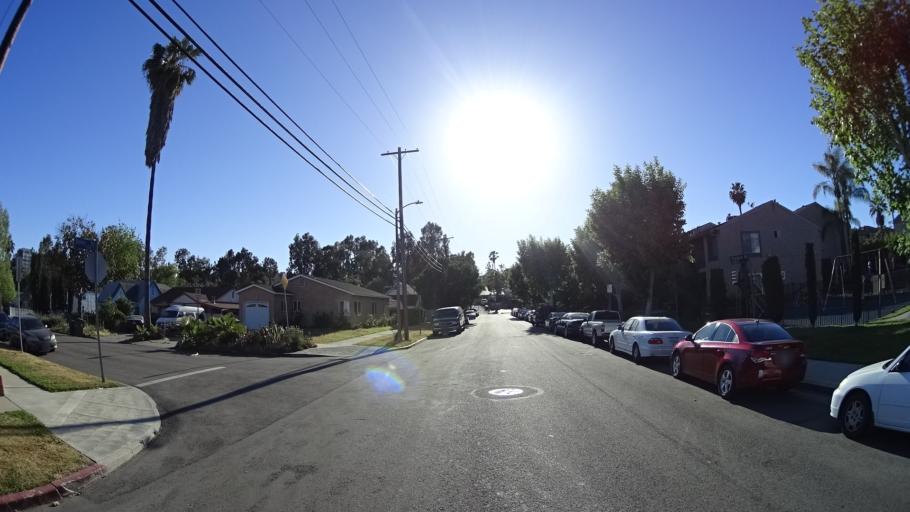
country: US
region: California
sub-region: Los Angeles County
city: Belvedere
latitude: 34.0720
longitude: -118.1632
